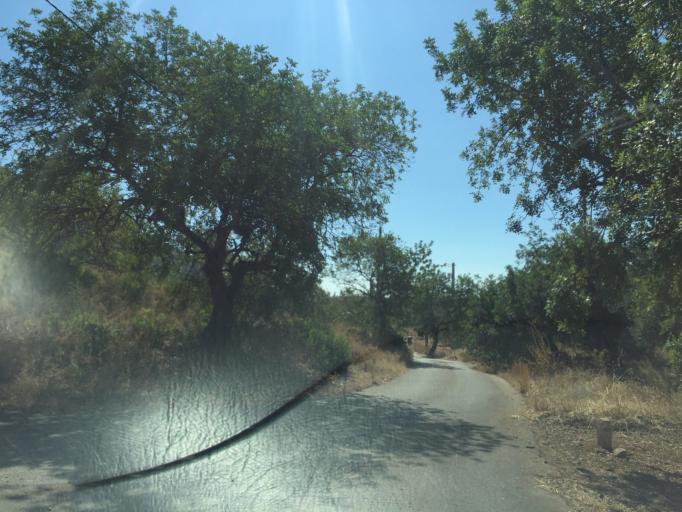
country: PT
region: Faro
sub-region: Loule
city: Vilamoura
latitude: 37.1168
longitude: -8.0808
